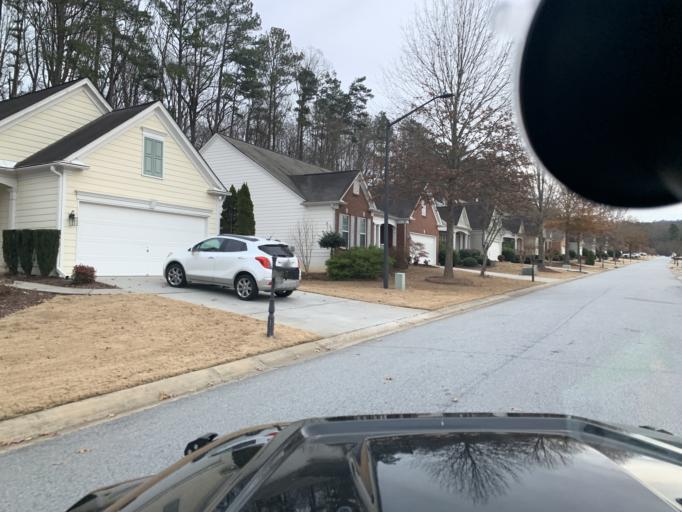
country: US
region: Georgia
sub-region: Cherokee County
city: Woodstock
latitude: 34.0899
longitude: -84.4544
